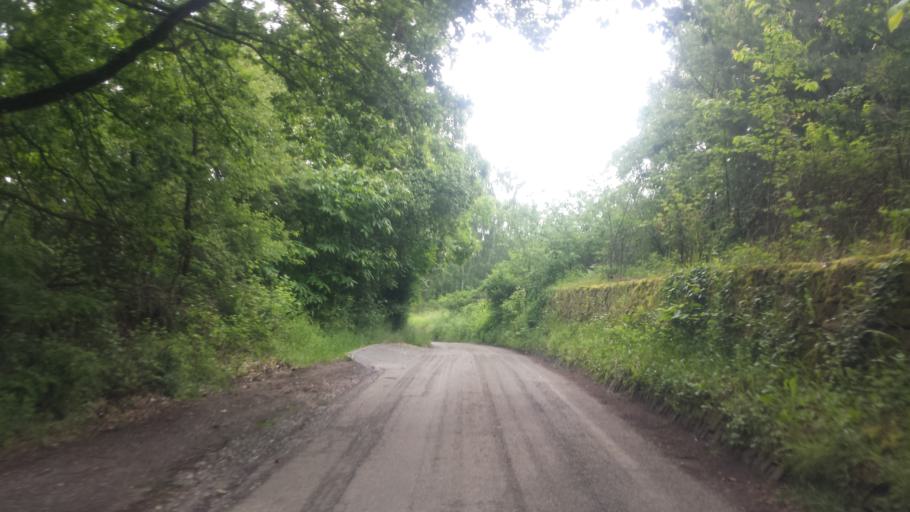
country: DE
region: Rheinland-Pfalz
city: Bad Duerkheim
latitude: 49.4491
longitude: 8.1632
